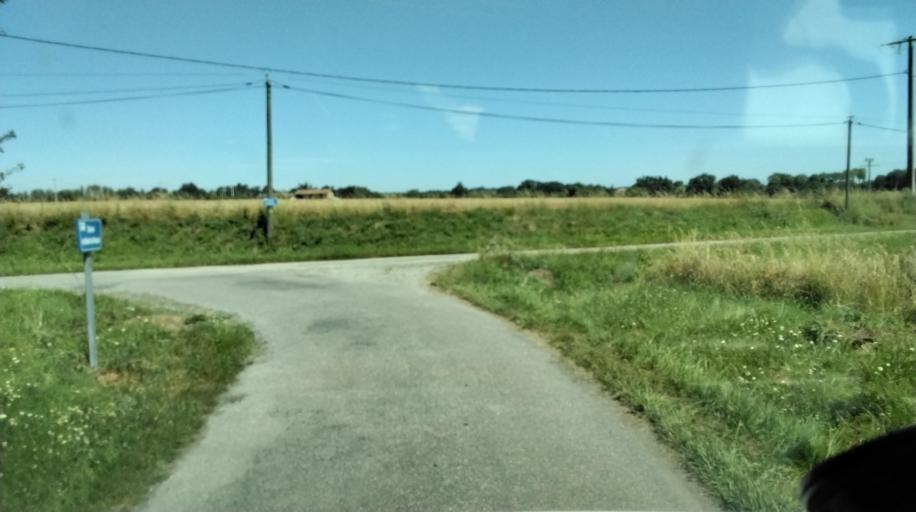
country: FR
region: Midi-Pyrenees
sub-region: Departement de la Haute-Garonne
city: Sainte-Foy-de-Peyrolieres
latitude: 43.4853
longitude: 1.1341
